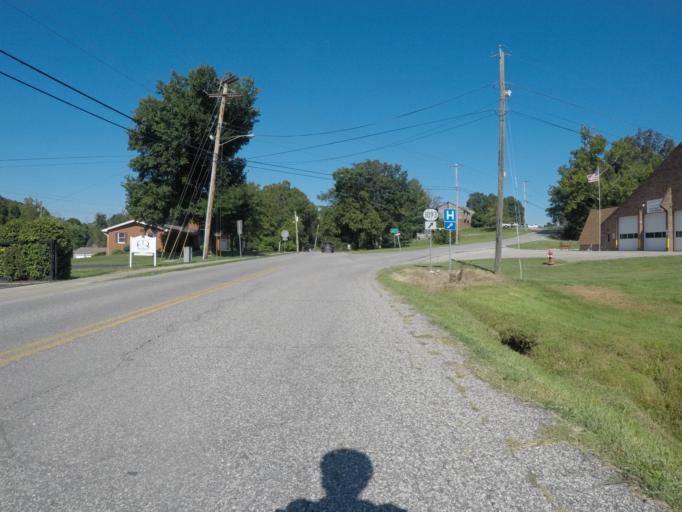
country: US
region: Kentucky
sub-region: Greenup County
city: Russell
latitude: 38.5057
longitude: -82.6943
